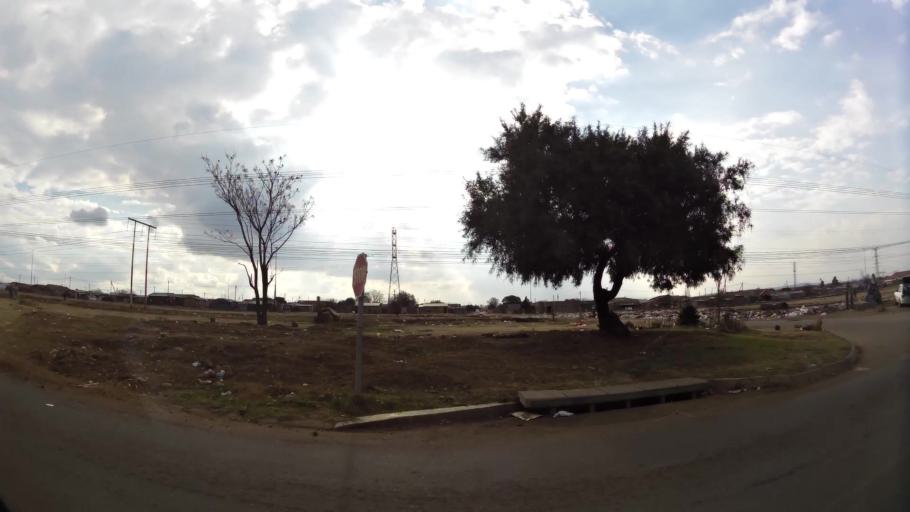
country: ZA
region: Gauteng
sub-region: Sedibeng District Municipality
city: Vanderbijlpark
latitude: -26.6779
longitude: 27.8743
